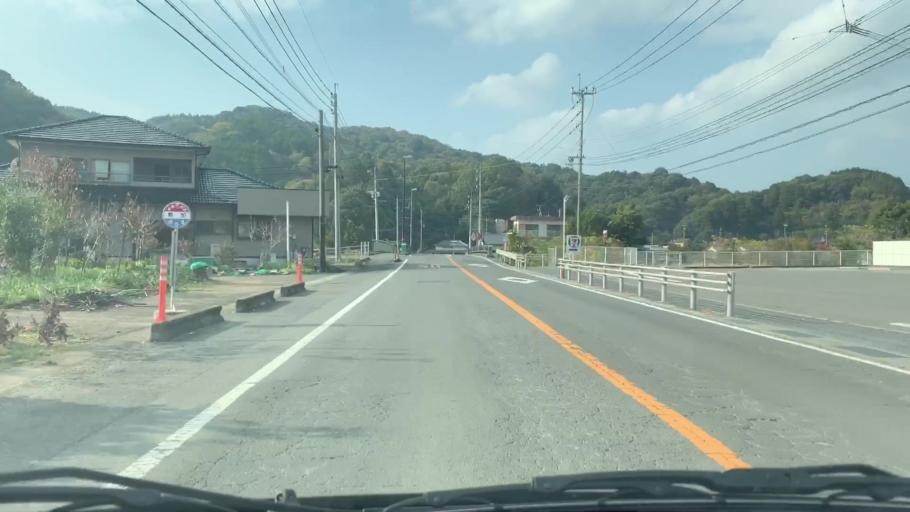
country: JP
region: Nagasaki
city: Sasebo
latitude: 32.9876
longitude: 129.7403
